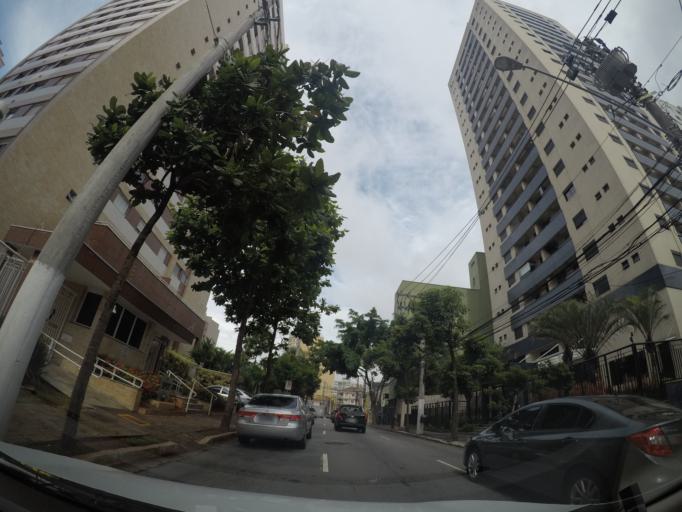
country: BR
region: Sao Paulo
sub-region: Sao Paulo
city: Sao Paulo
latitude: -23.5909
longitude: -46.6340
